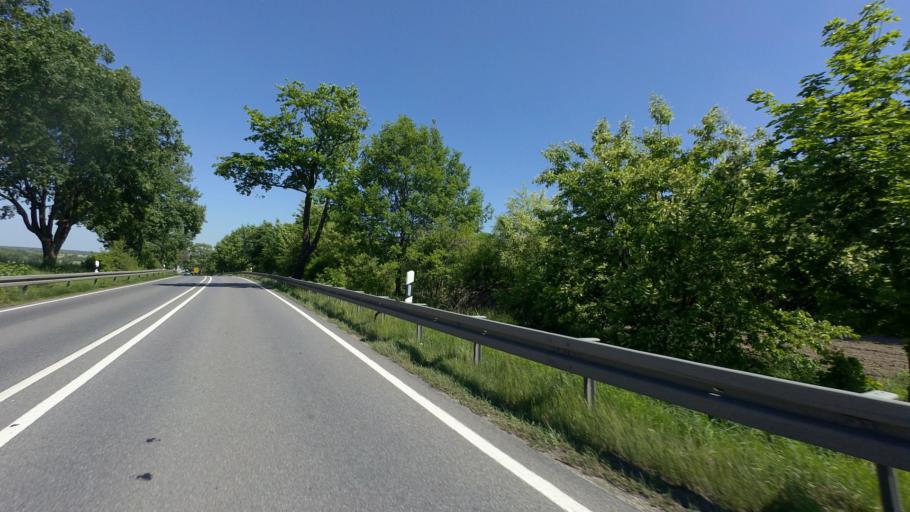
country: DE
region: Brandenburg
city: Spremberg
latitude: 51.6539
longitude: 14.3611
